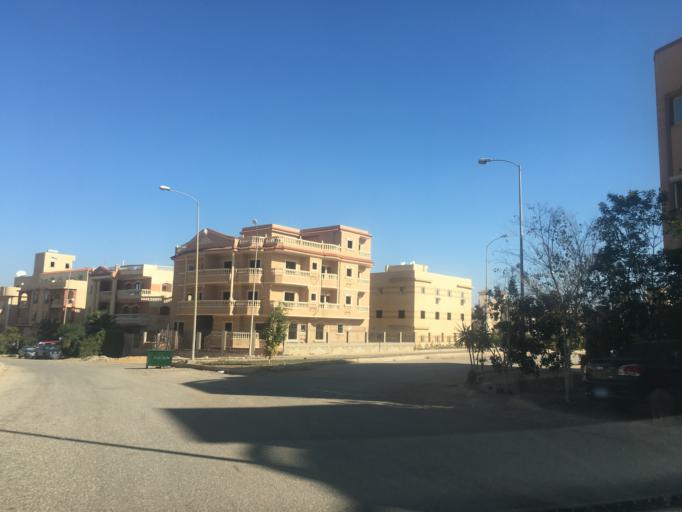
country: EG
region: Al Jizah
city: Awsim
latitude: 30.0270
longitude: 30.9833
